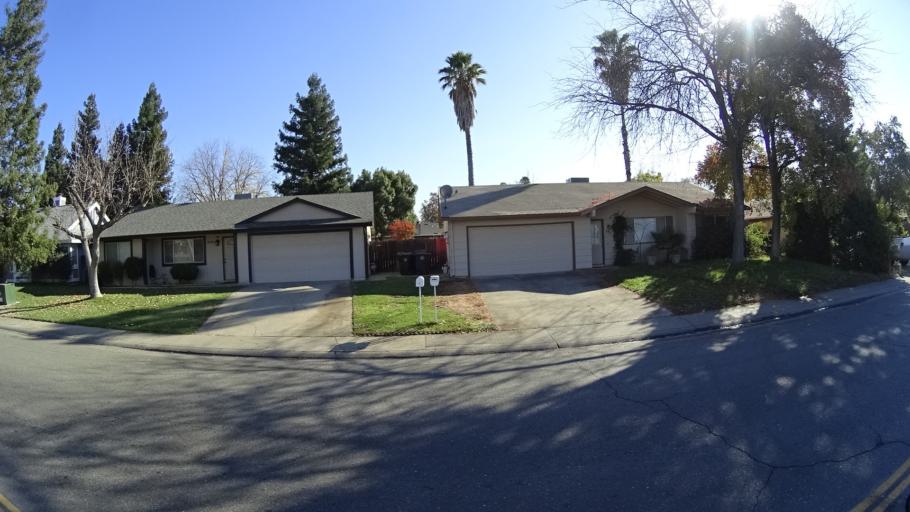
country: US
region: California
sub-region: Sacramento County
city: Antelope
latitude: 38.7171
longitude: -121.3054
